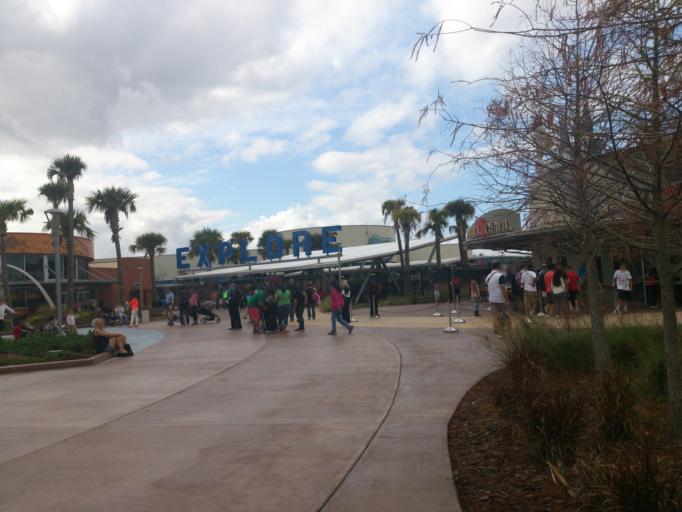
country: US
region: Florida
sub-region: Brevard County
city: Merritt Island
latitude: 28.5230
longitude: -80.6819
